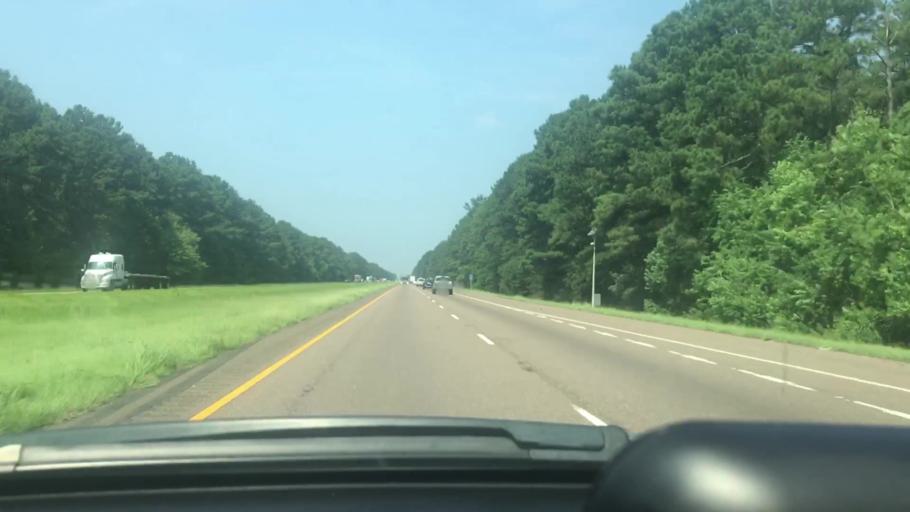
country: US
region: Louisiana
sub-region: Livingston Parish
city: Livingston
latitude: 30.4743
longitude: -90.7560
